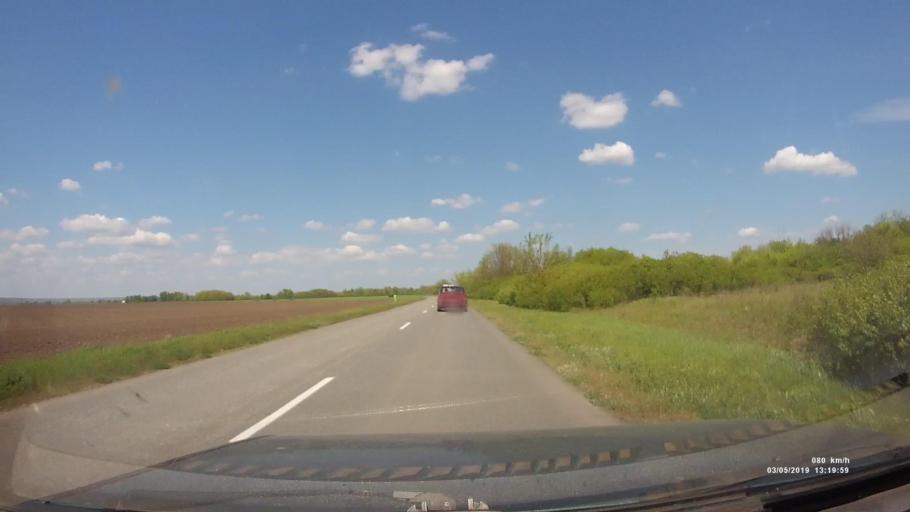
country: RU
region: Rostov
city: Semikarakorsk
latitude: 47.5415
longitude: 40.7530
